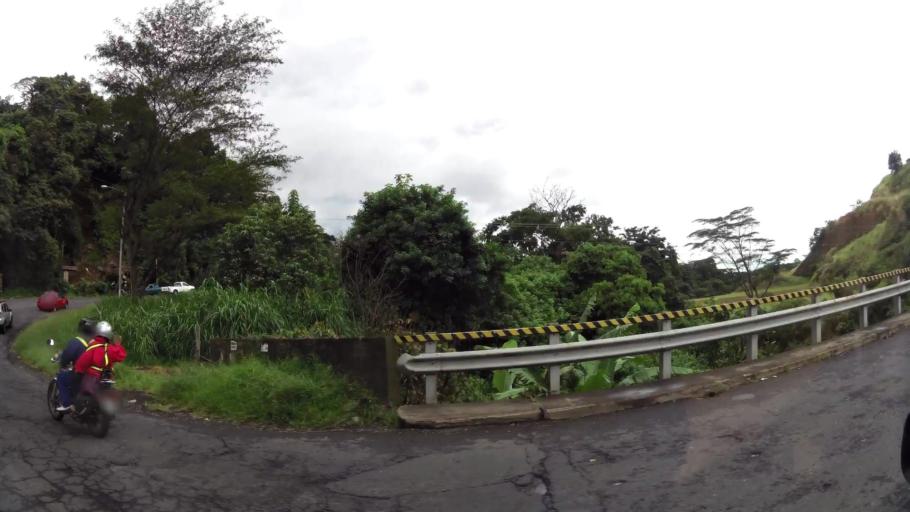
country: CR
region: San Jose
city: San Juan
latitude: 9.9682
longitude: -84.0847
